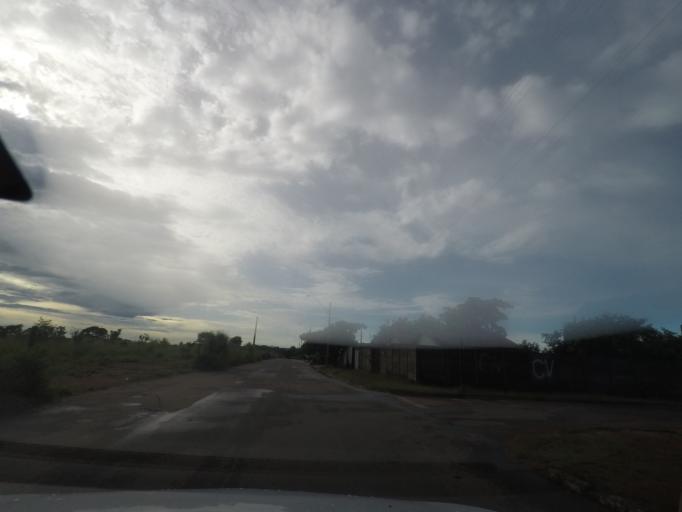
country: BR
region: Goias
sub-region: Aparecida De Goiania
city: Aparecida de Goiania
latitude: -16.7772
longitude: -49.3860
